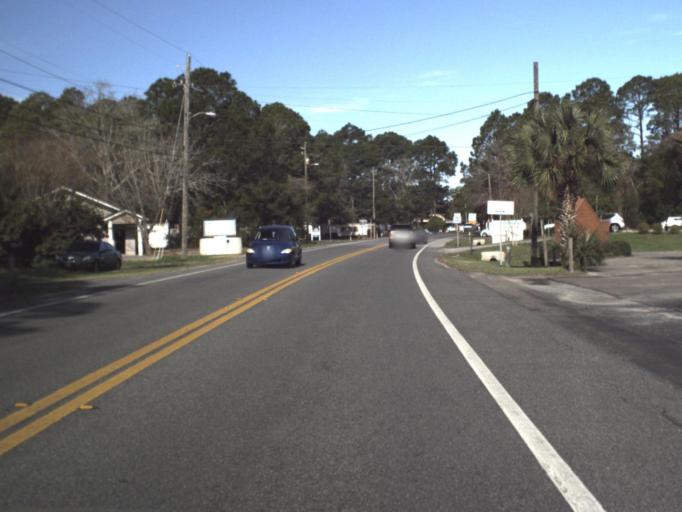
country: US
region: Florida
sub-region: Bay County
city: Panama City
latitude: 30.1790
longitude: -85.6635
